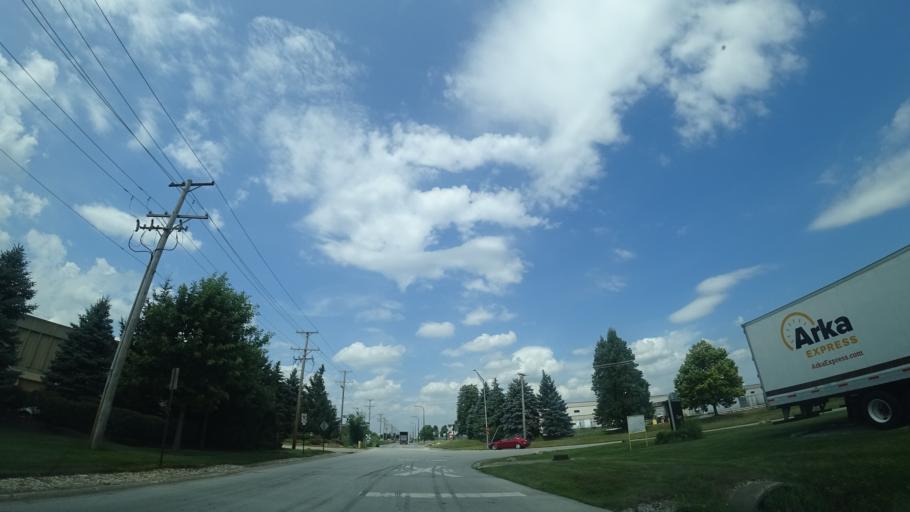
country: US
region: Illinois
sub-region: Cook County
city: Crestwood
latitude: 41.6718
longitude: -87.7585
